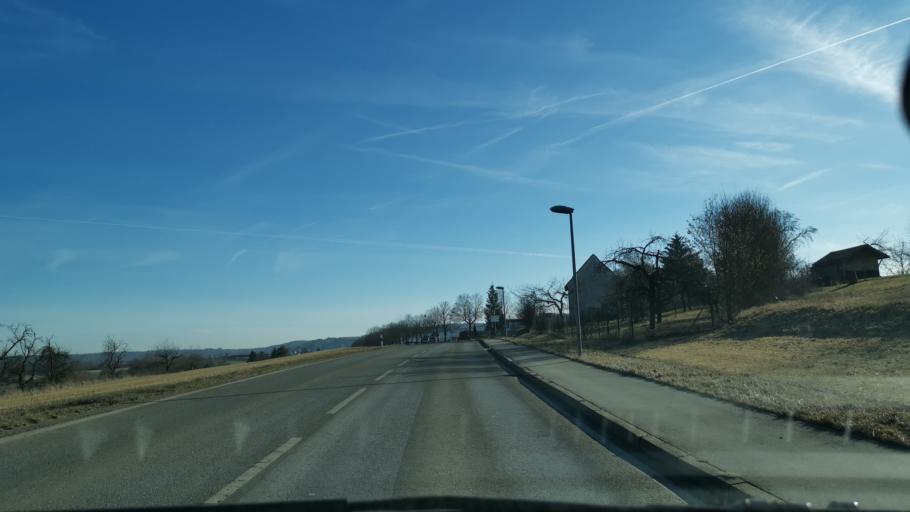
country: DE
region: Baden-Wuerttemberg
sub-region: Regierungsbezirk Stuttgart
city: Nufringen
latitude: 48.6209
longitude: 8.9000
